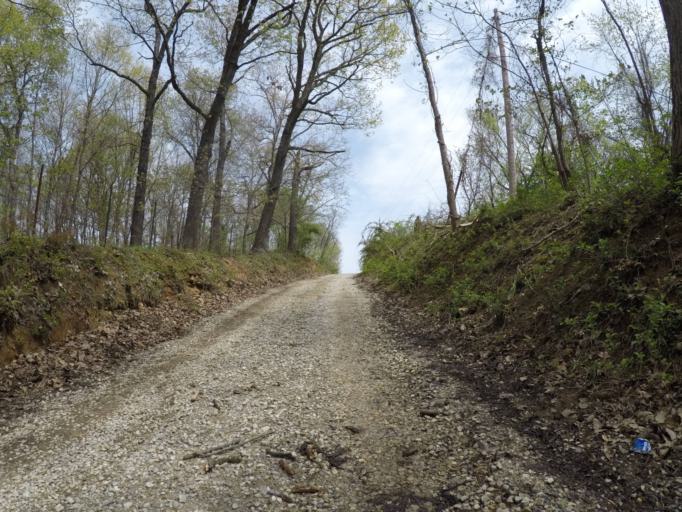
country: US
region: West Virginia
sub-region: Wayne County
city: Lavalette
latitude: 38.3683
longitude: -82.4805
